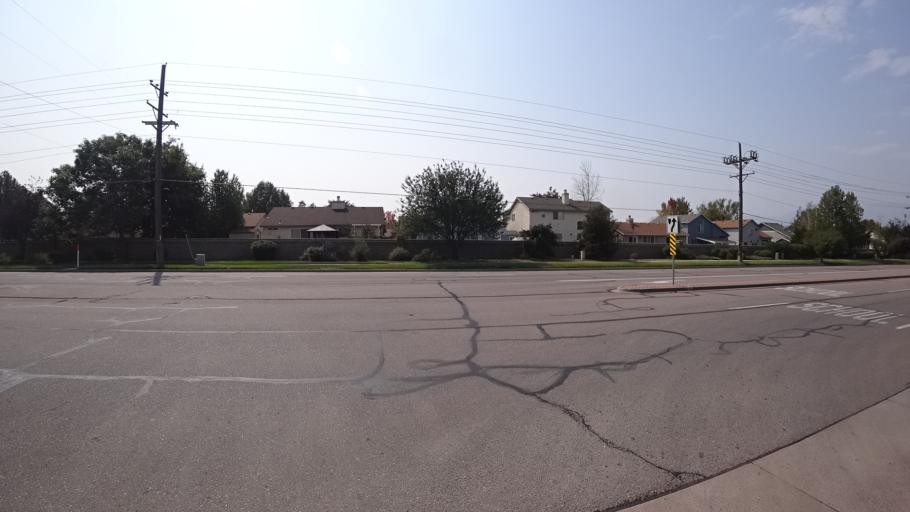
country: US
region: Colorado
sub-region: El Paso County
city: Cimarron Hills
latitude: 38.8254
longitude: -104.7365
